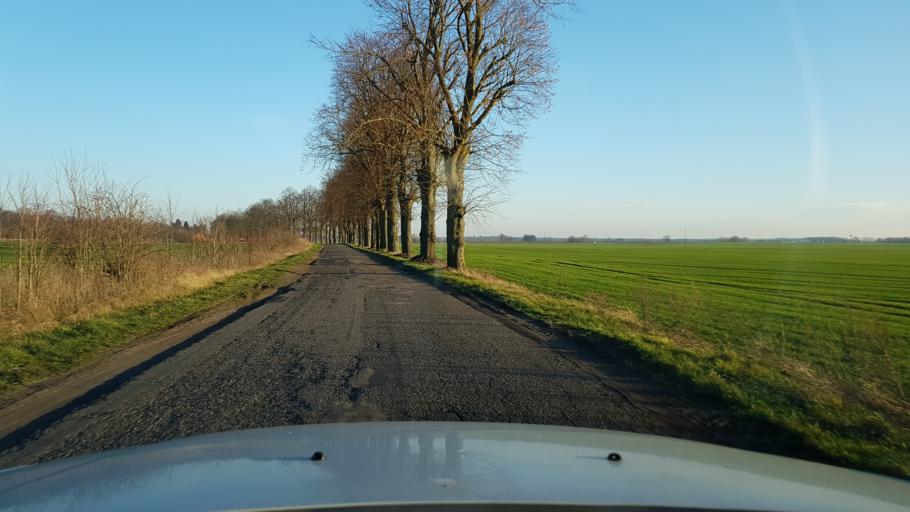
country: PL
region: West Pomeranian Voivodeship
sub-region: Powiat gryficki
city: Brojce
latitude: 53.9899
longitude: 15.3346
